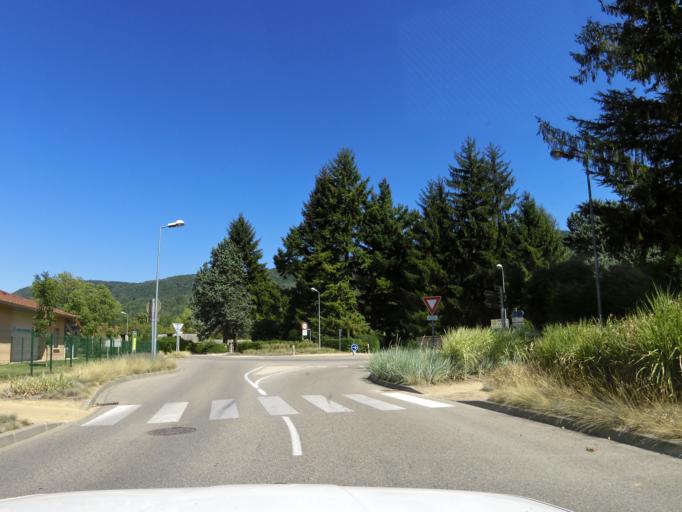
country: FR
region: Rhone-Alpes
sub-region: Departement de l'Ain
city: Lagnieu
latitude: 45.8935
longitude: 5.3471
